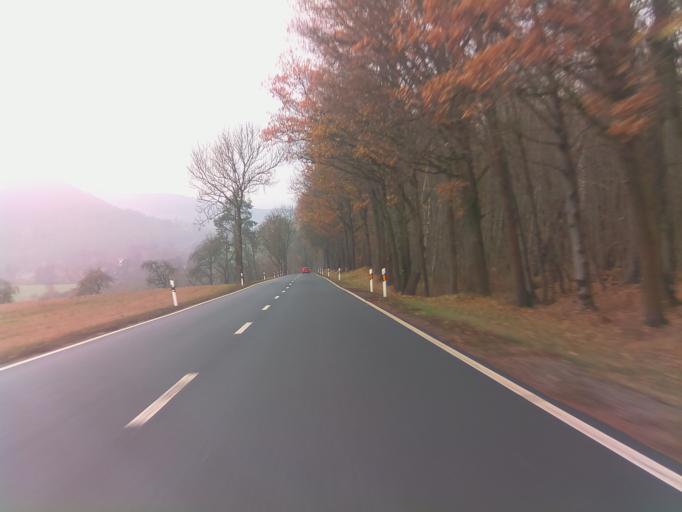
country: DE
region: Thuringia
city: Ehrenberg
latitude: 50.4855
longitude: 10.6449
